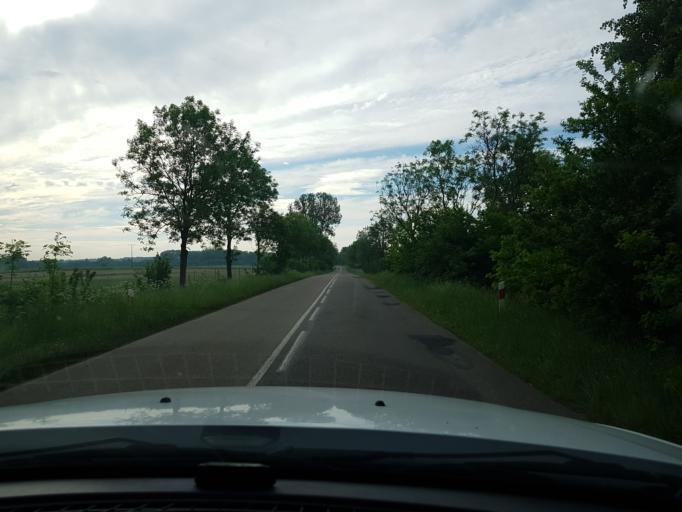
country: PL
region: West Pomeranian Voivodeship
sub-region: Powiat stargardzki
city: Chociwel
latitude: 53.4658
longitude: 15.3647
